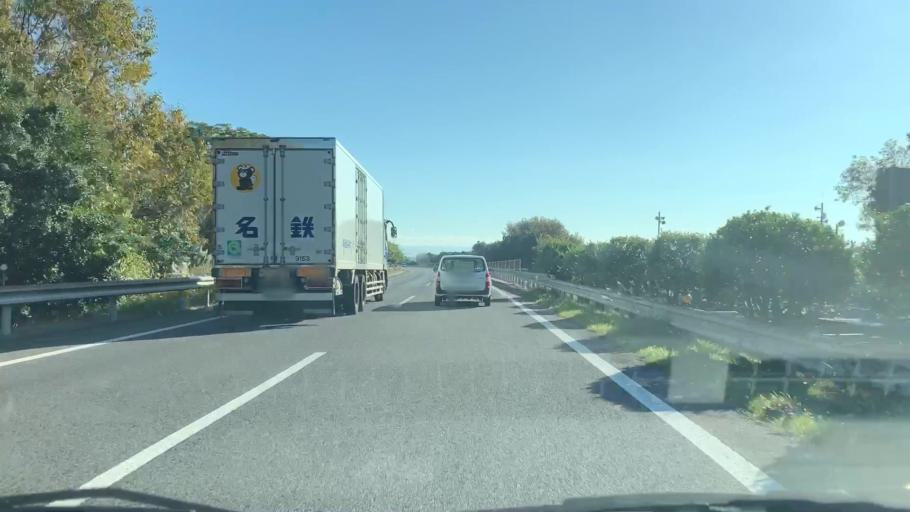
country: JP
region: Saga Prefecture
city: Saga-shi
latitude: 33.3072
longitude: 130.2295
